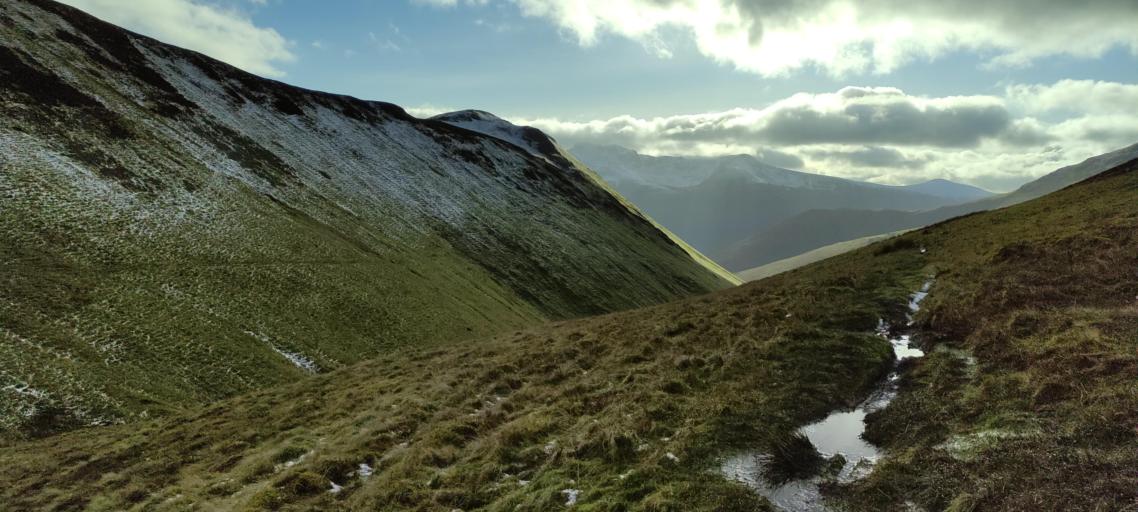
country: GB
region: England
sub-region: Cumbria
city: Keswick
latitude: 54.5686
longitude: -3.2334
